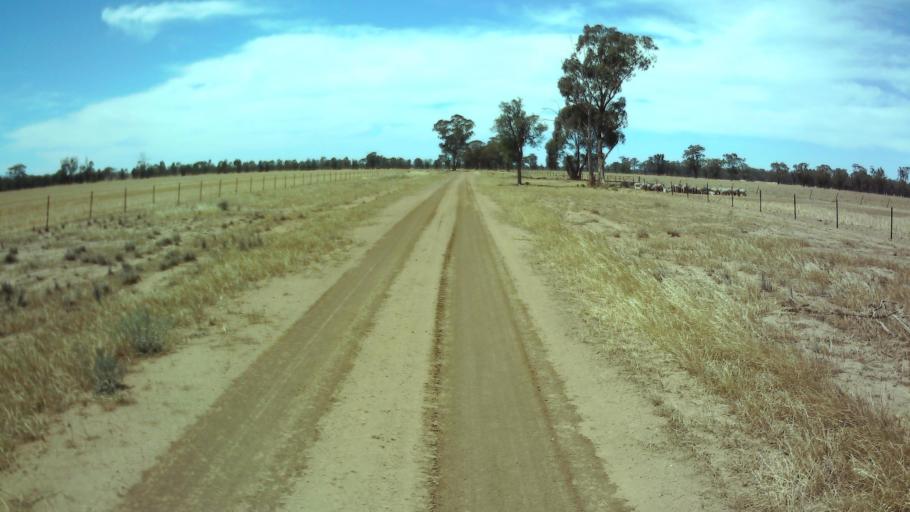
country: AU
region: New South Wales
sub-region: Weddin
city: Grenfell
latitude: -33.8980
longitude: 147.8033
